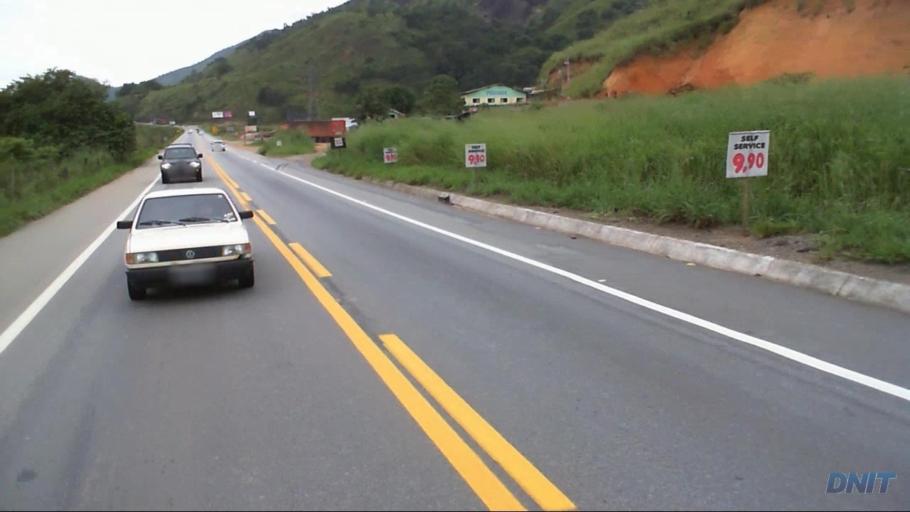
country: BR
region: Minas Gerais
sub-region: Timoteo
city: Timoteo
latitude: -19.5875
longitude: -42.7331
